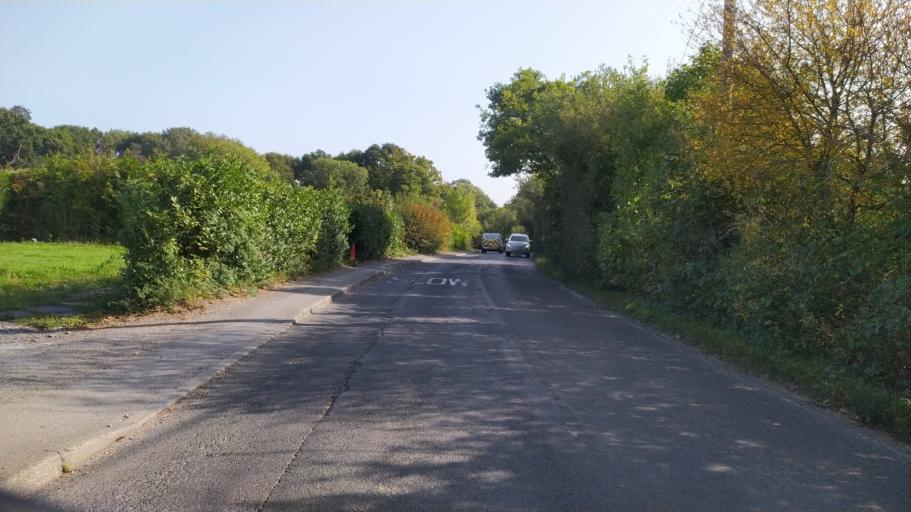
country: GB
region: England
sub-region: Hampshire
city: Hedge End
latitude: 50.9190
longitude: -1.2880
